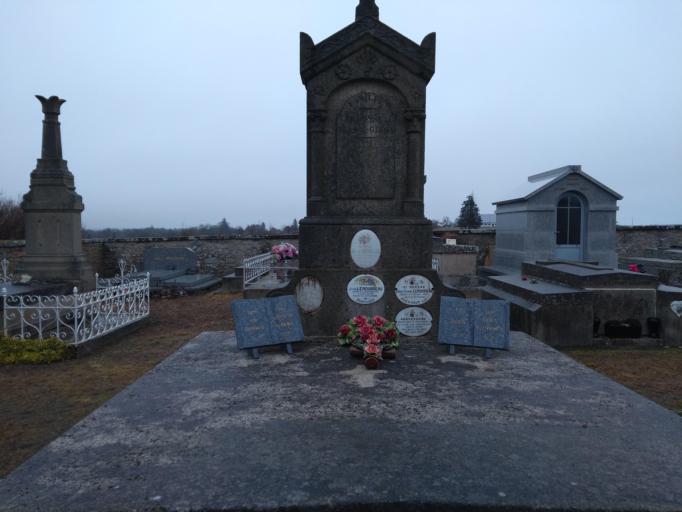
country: FR
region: Limousin
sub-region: Departement de la Creuse
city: Banize
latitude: 45.7730
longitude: 2.0740
